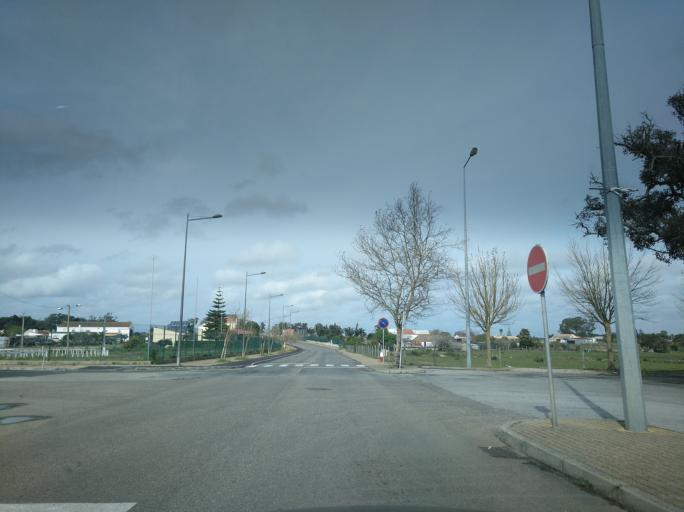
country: PT
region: Setubal
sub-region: Grandola
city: Grandola
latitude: 38.1851
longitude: -8.5640
